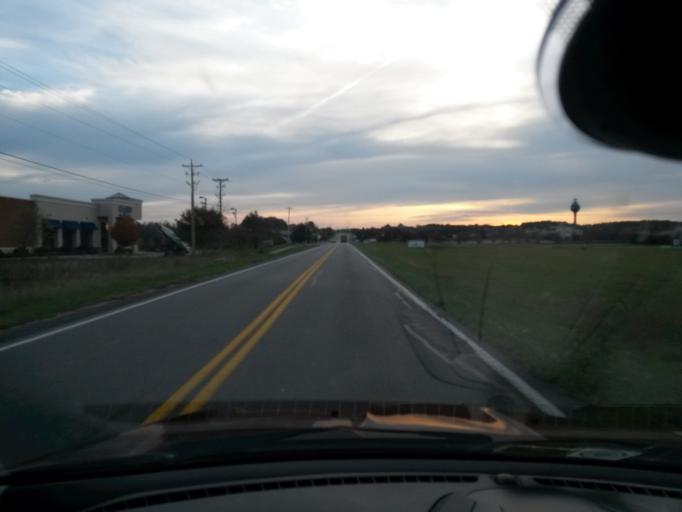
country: US
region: Virginia
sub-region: Franklin County
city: North Shore
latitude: 37.1205
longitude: -79.7252
